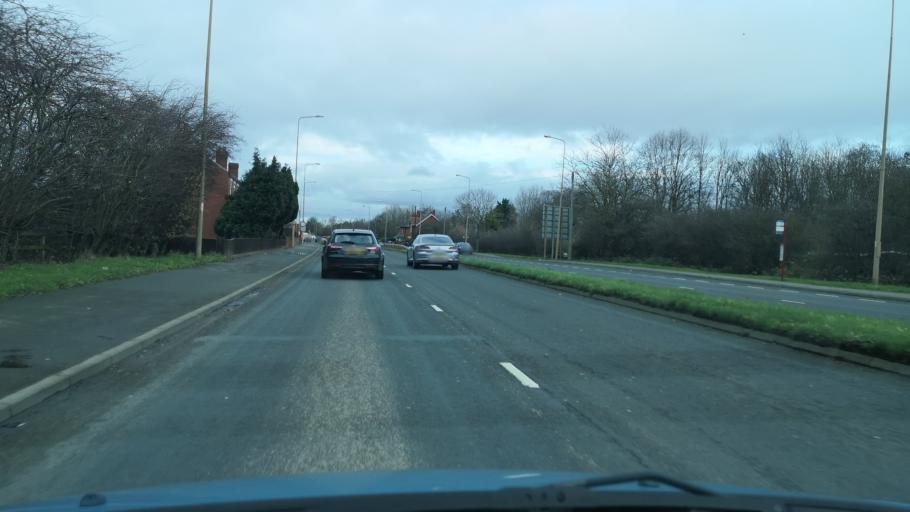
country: GB
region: England
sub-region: City and Borough of Wakefield
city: Crigglestone
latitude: 53.6595
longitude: -1.5115
